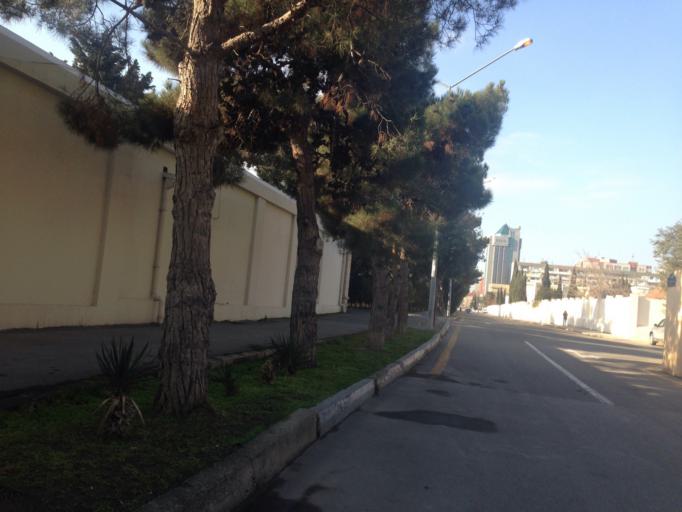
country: AZ
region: Baki
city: Baku
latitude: 40.4084
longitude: 49.8524
